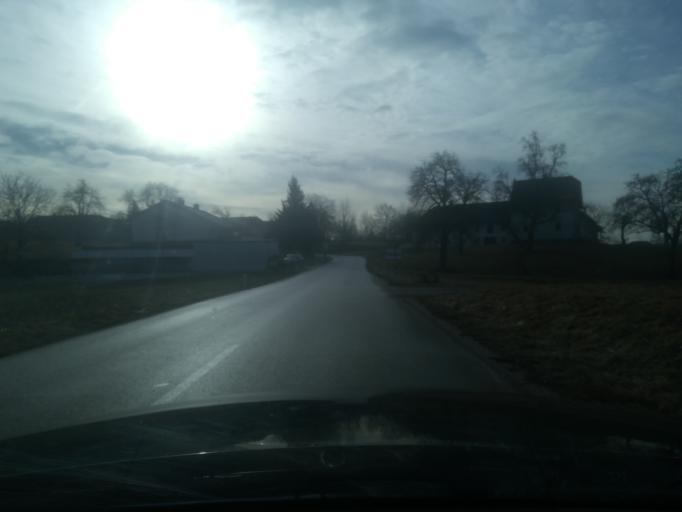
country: AT
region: Upper Austria
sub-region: Wels-Land
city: Holzhausen
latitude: 48.2677
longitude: 14.1152
